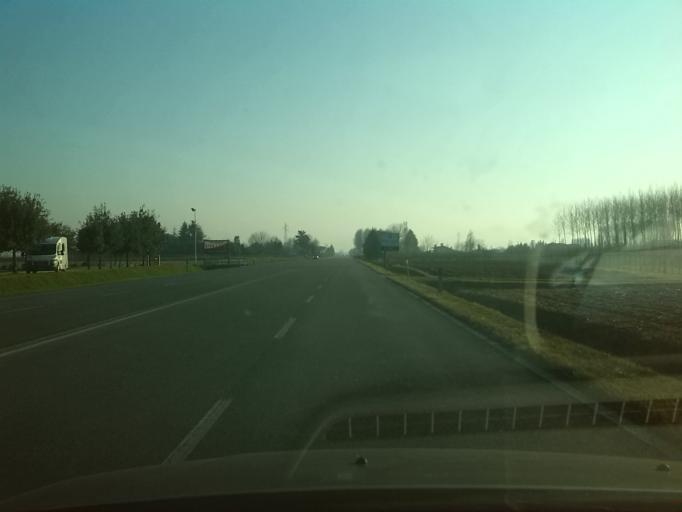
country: IT
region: Friuli Venezia Giulia
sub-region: Provincia di Udine
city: Pertegada
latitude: 45.7435
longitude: 13.0376
